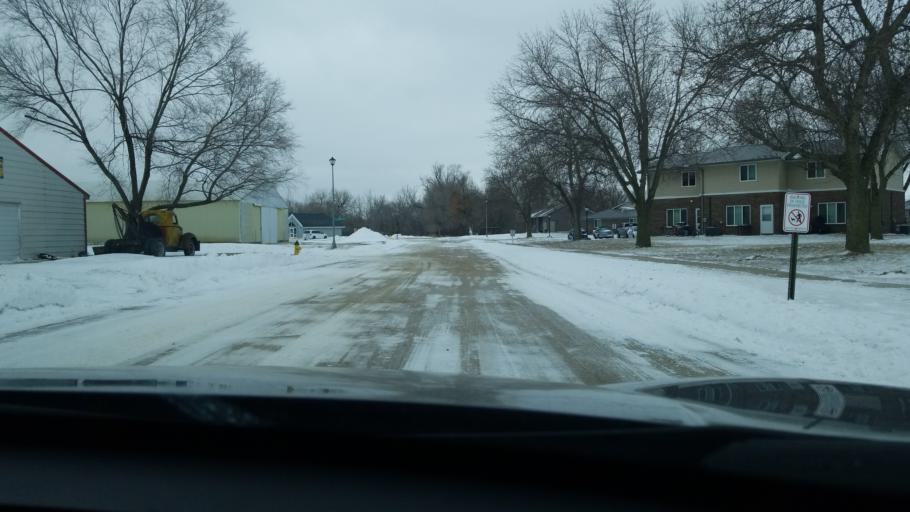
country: US
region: Iowa
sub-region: Lyon County
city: Rock Rapids
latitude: 43.4317
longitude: -96.1582
